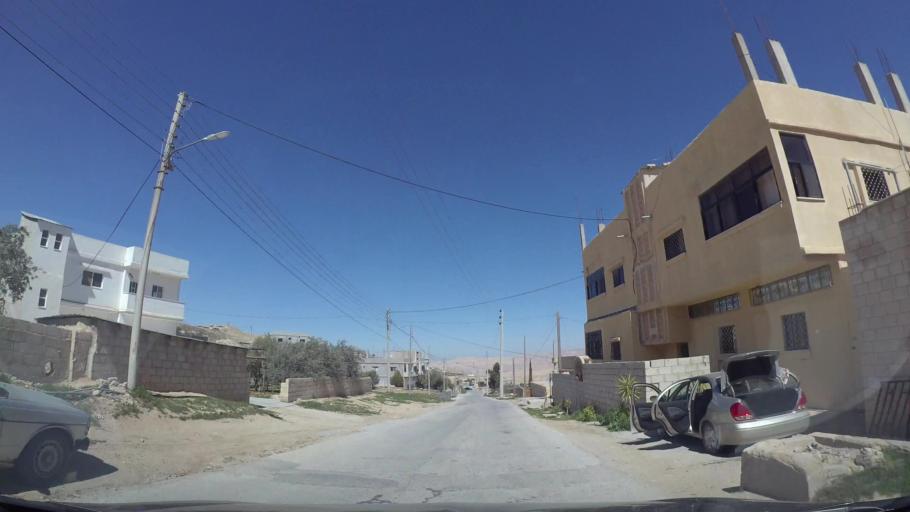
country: JO
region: Tafielah
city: At Tafilah
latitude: 30.8283
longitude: 35.5797
